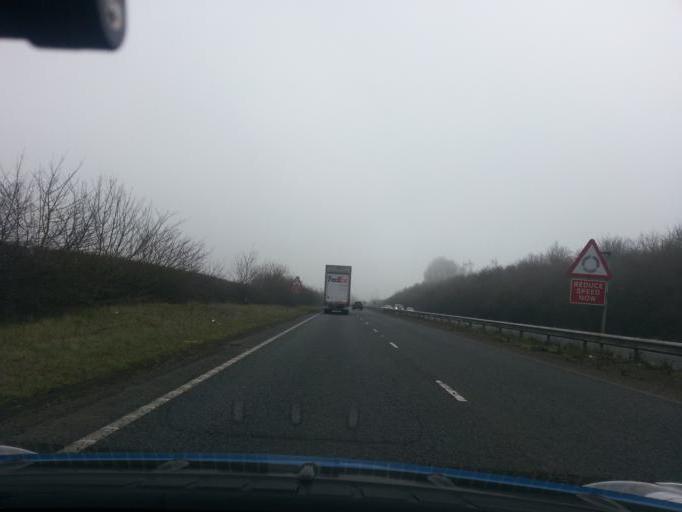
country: GB
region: England
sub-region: Oxfordshire
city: Frilford
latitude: 51.6843
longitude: -1.4204
